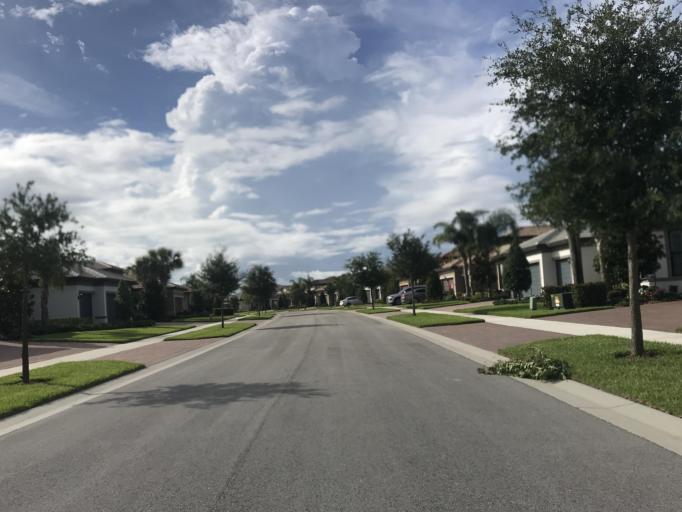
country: US
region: Florida
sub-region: Indian River County
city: Gifford
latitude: 27.6891
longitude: -80.4291
